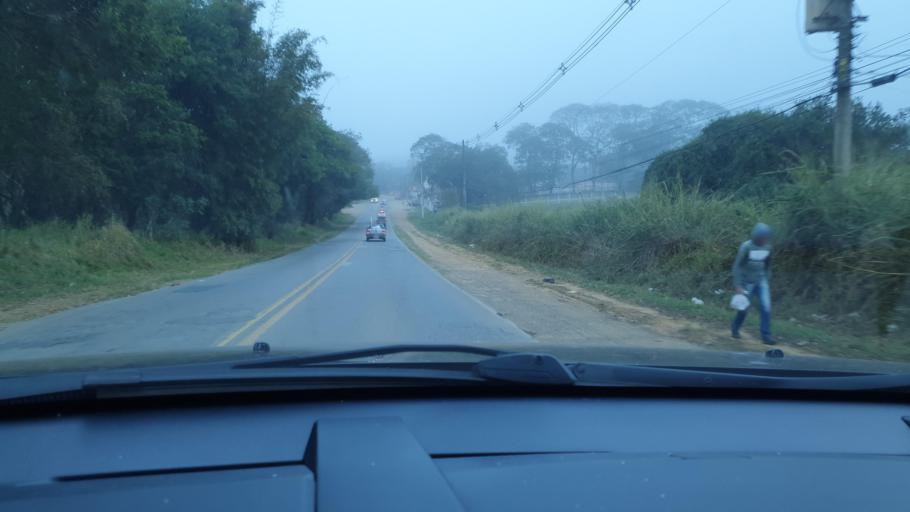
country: BR
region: Sao Paulo
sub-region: Ibiuna
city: Ibiuna
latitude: -23.6705
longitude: -47.2328
